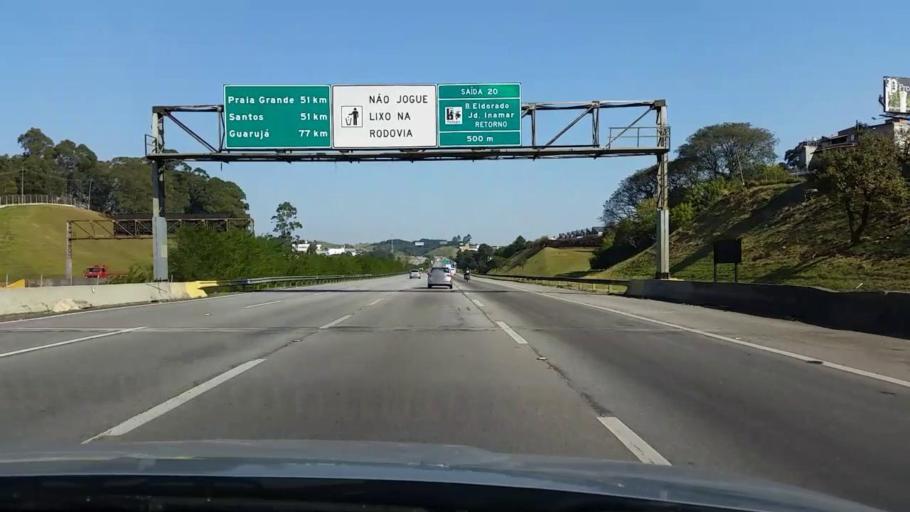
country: BR
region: Sao Paulo
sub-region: Diadema
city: Diadema
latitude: -23.7103
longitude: -46.6040
